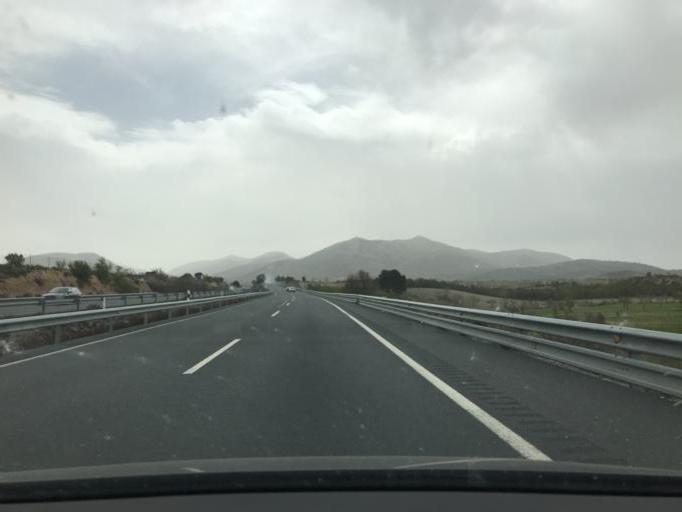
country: ES
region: Andalusia
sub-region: Provincia de Granada
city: Gor
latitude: 37.3949
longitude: -2.9742
